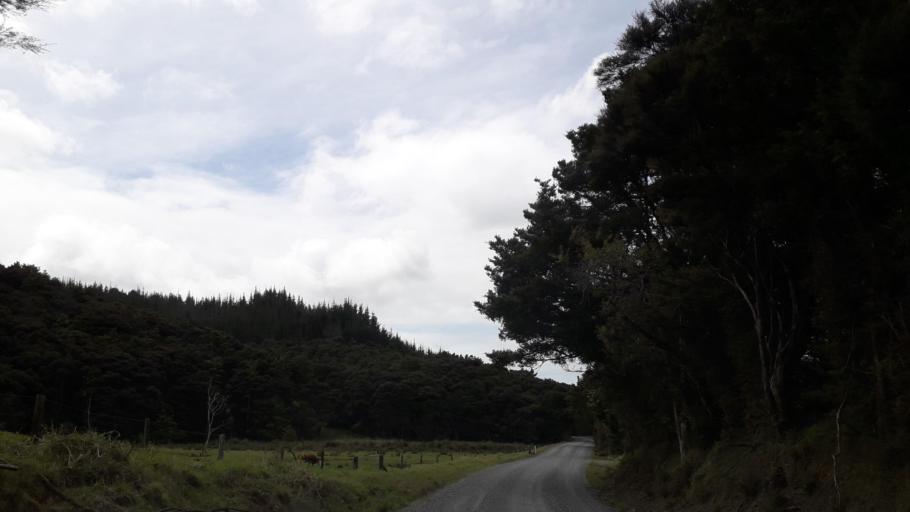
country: NZ
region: Northland
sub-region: Far North District
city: Taipa
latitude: -35.0498
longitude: 173.5586
